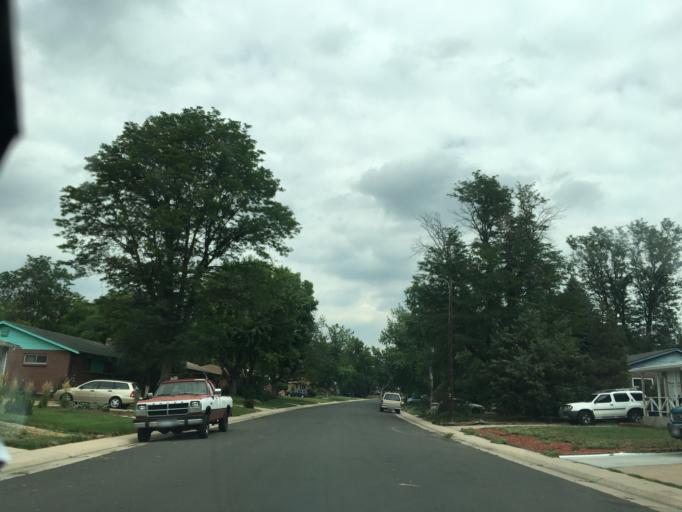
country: US
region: Colorado
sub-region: Arapahoe County
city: Sheridan
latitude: 39.6577
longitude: -105.0491
